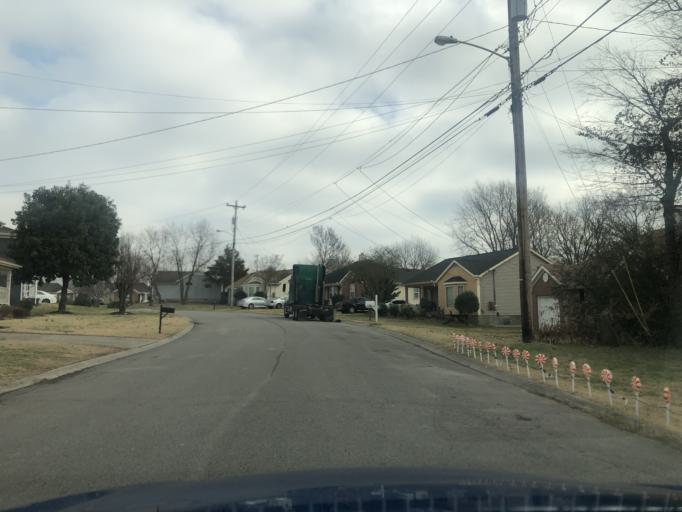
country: US
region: Tennessee
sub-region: Davidson County
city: Oak Hill
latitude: 36.0905
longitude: -86.7101
